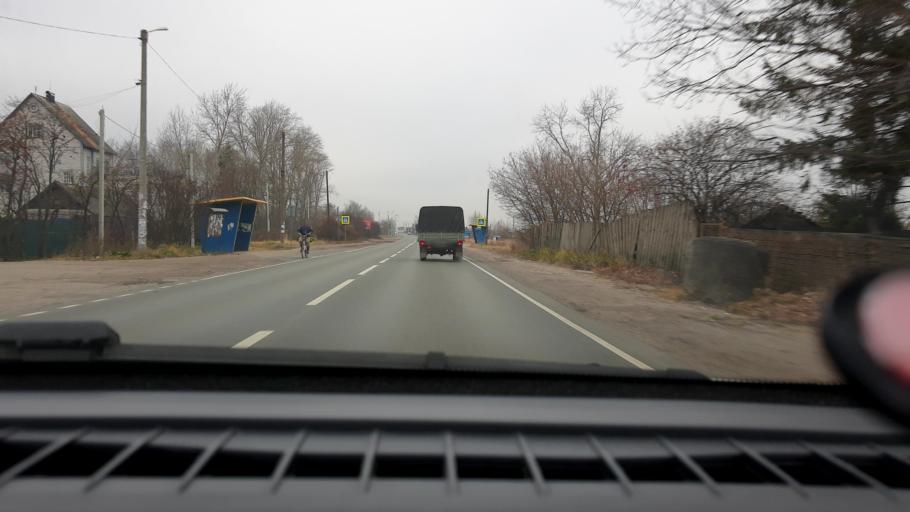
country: RU
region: Nizjnij Novgorod
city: Gidrotorf
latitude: 56.5477
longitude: 43.5246
